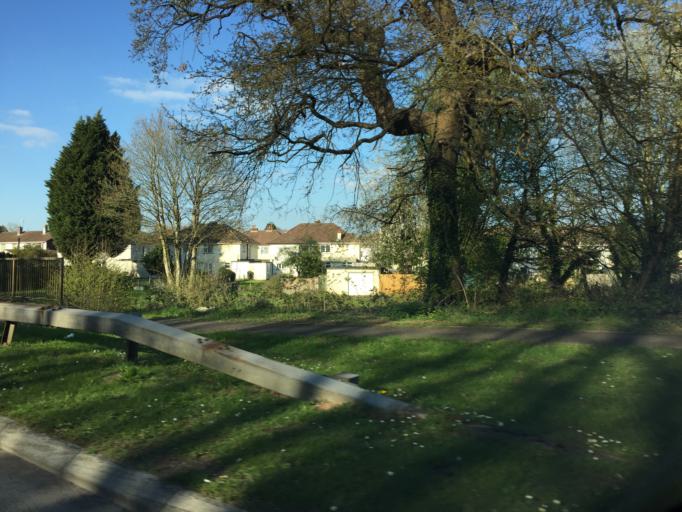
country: GB
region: Wales
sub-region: Torfaen County Borough
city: Cwmbran
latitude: 51.6378
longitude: -3.0208
